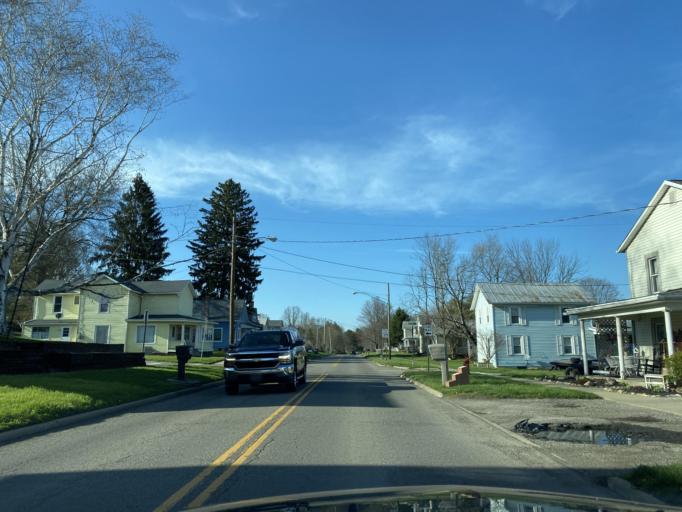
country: US
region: Ohio
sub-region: Wayne County
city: Shreve
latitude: 40.6872
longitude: -82.0223
